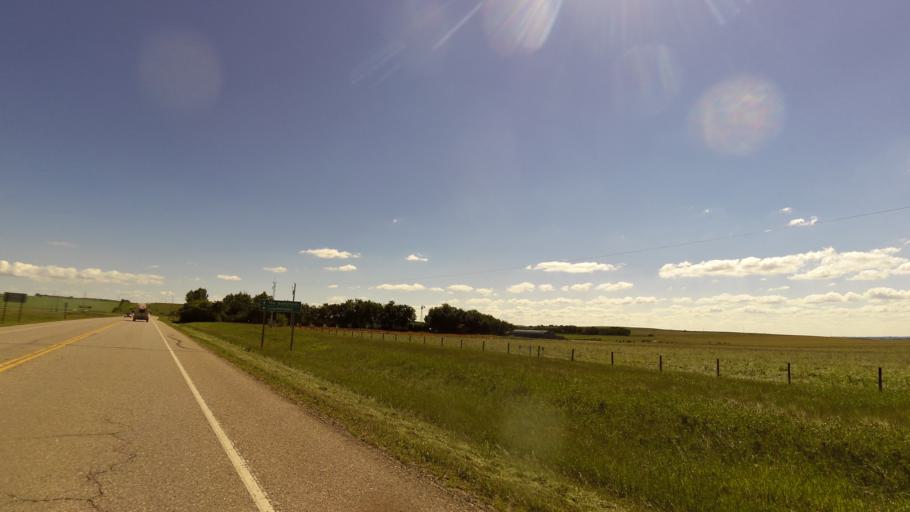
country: CA
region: Saskatchewan
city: Lloydminster
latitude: 52.8417
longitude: -110.0226
